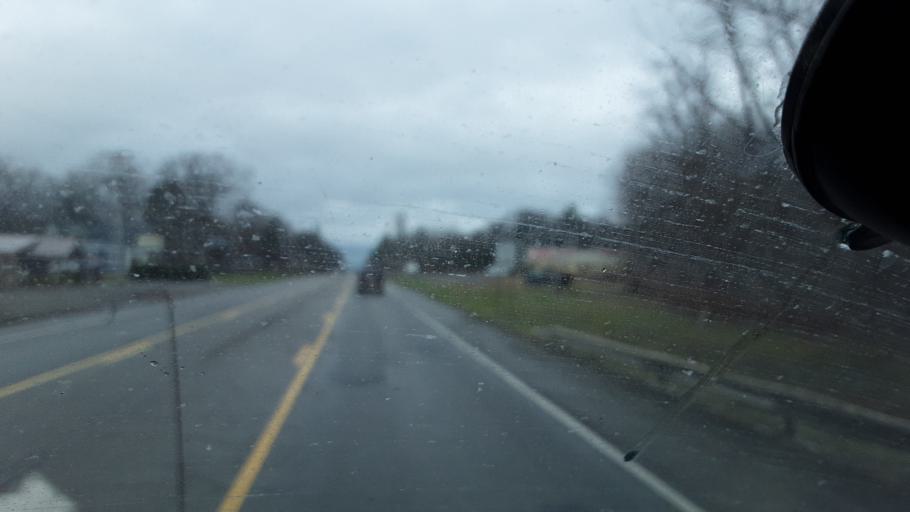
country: US
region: New York
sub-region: Cattaraugus County
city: Yorkshire
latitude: 42.5163
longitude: -78.4782
